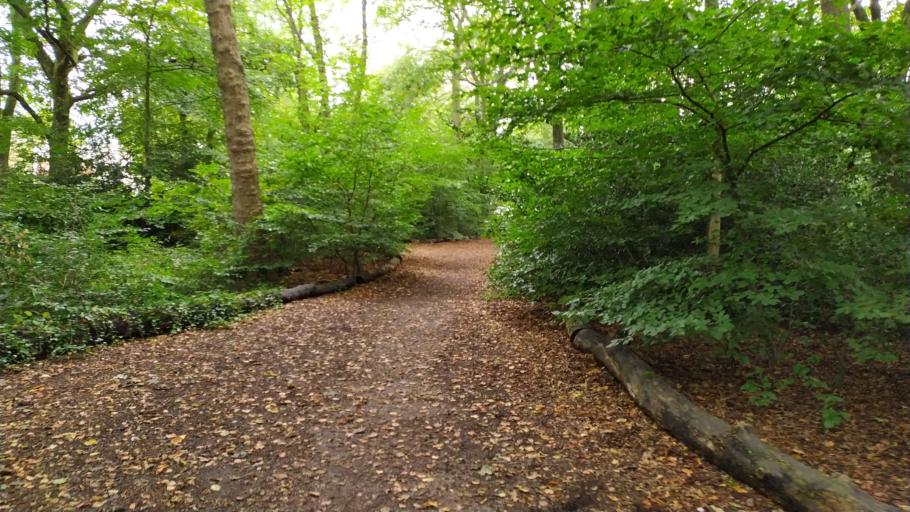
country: GB
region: England
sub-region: City and Borough of Leeds
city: Chapel Allerton
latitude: 53.8276
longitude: -1.5888
